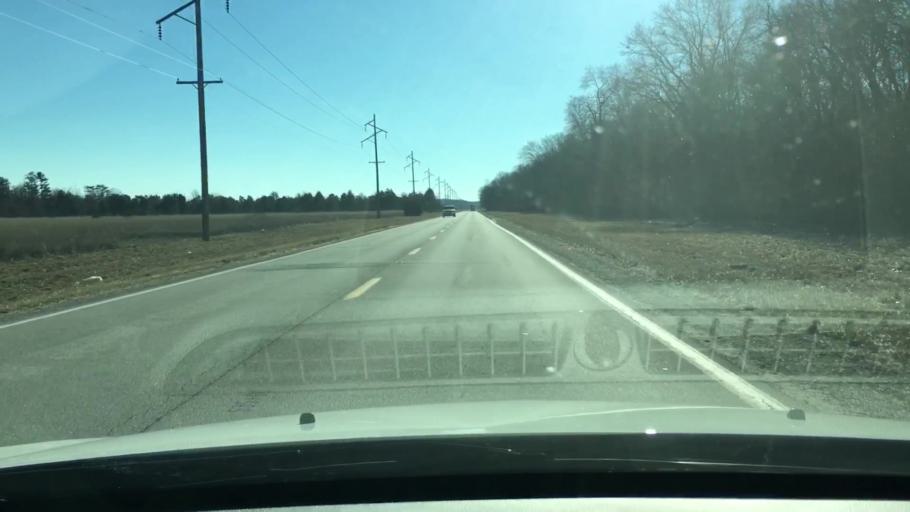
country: US
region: Illinois
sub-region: Morgan County
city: Meredosia
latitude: 39.8829
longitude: -90.5052
